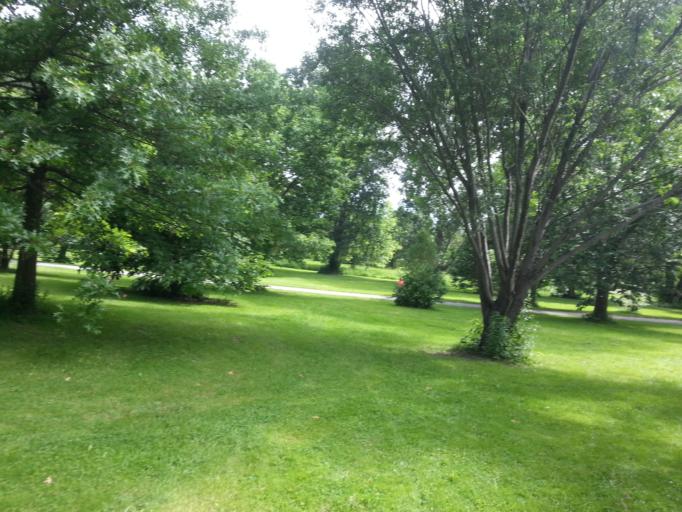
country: CA
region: Ontario
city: Ottawa
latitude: 45.3872
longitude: -75.7022
